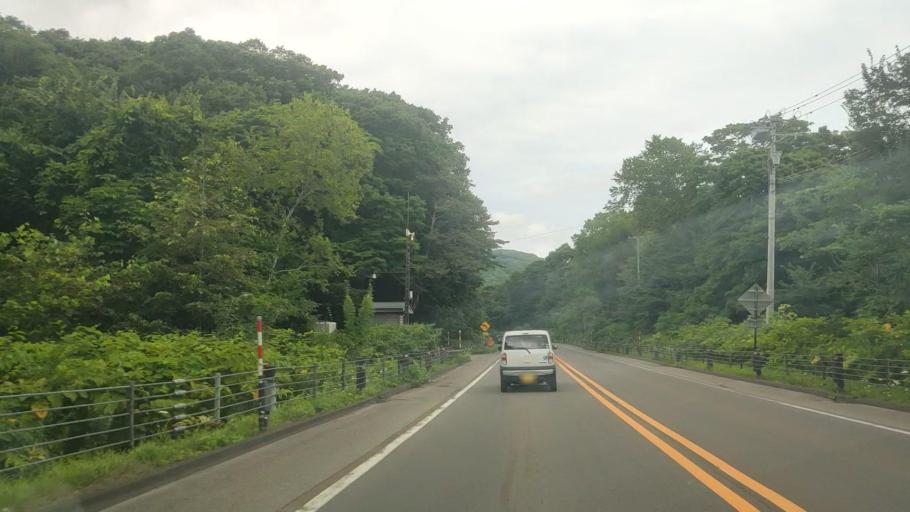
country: JP
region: Hokkaido
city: Nanae
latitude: 41.9709
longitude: 140.6507
